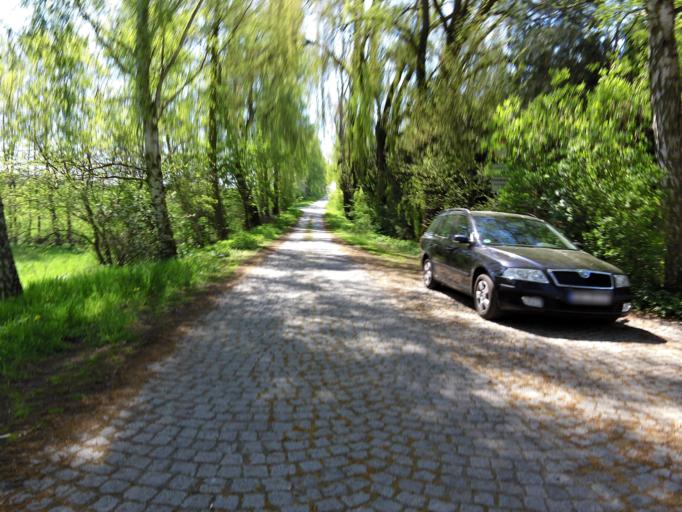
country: DE
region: Thuringia
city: Marksuhl
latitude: 50.9043
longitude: 10.2233
